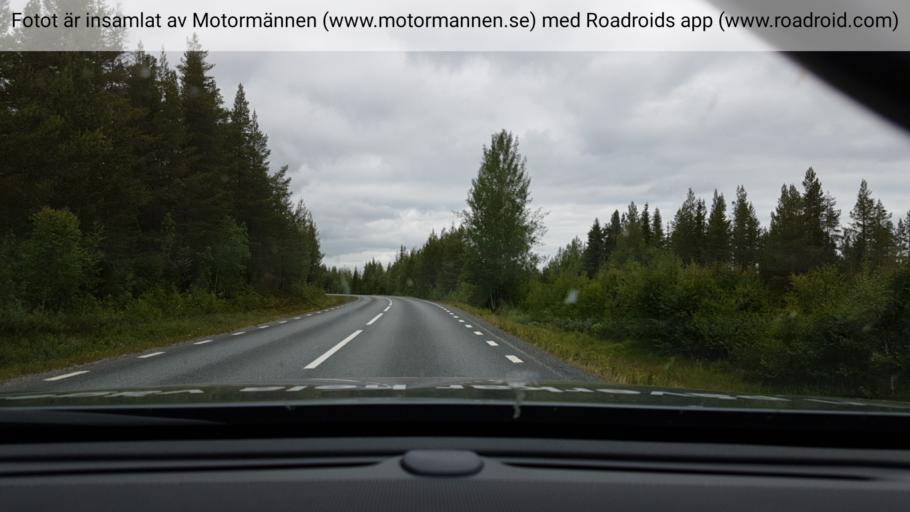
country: SE
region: Vaesterbotten
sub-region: Sorsele Kommun
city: Sorsele
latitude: 65.4050
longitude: 17.5742
